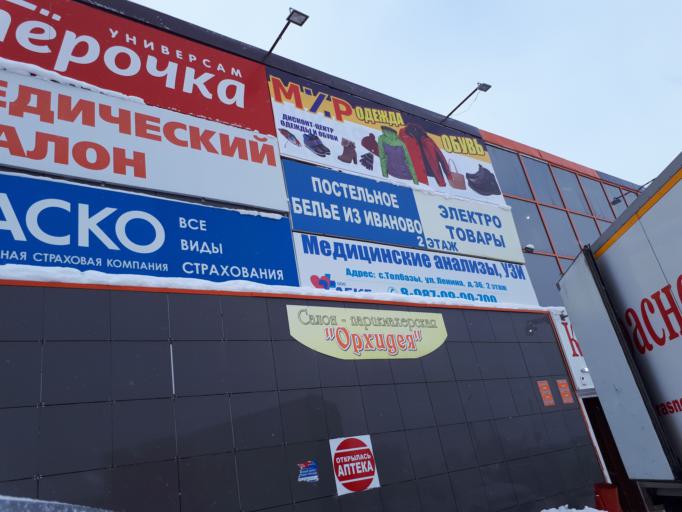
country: RU
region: Bashkortostan
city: Tolbazy
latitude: 54.0251
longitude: 55.8855
